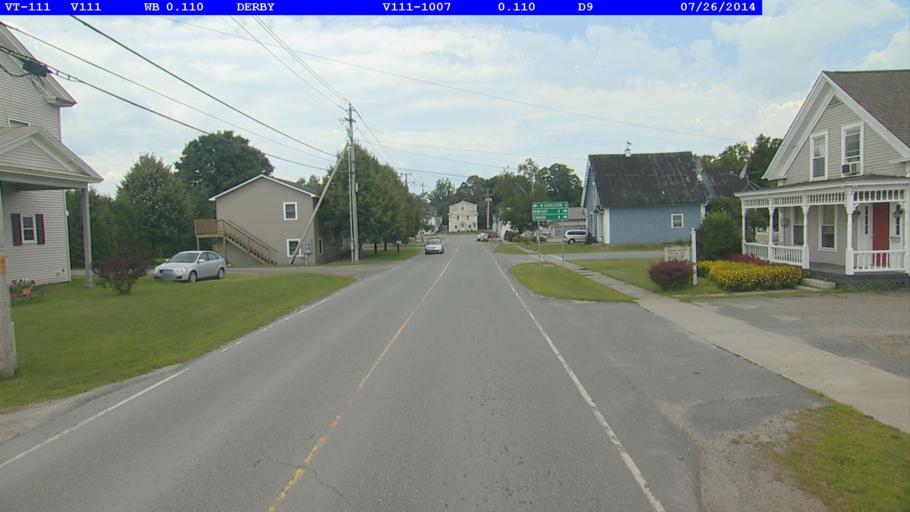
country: US
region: Vermont
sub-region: Orleans County
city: Newport
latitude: 44.9471
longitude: -72.1315
